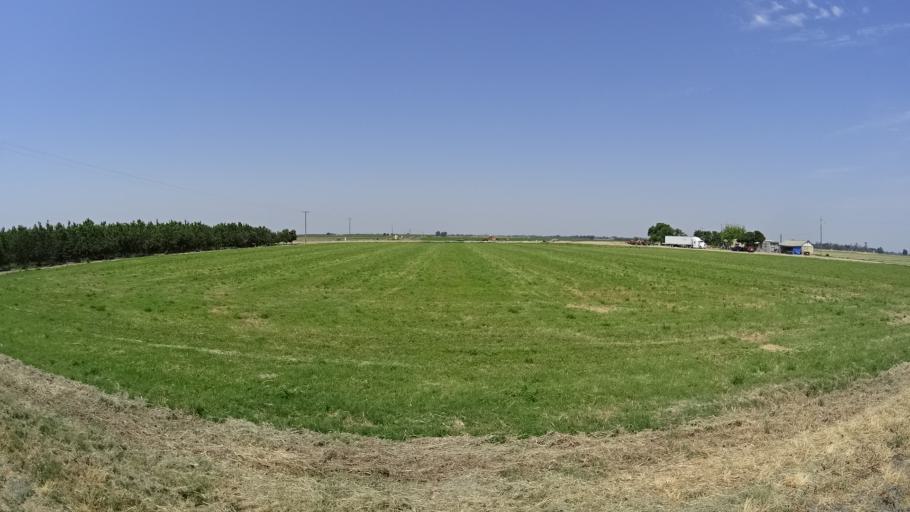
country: US
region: California
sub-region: Kings County
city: Armona
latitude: 36.3576
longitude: -119.7448
